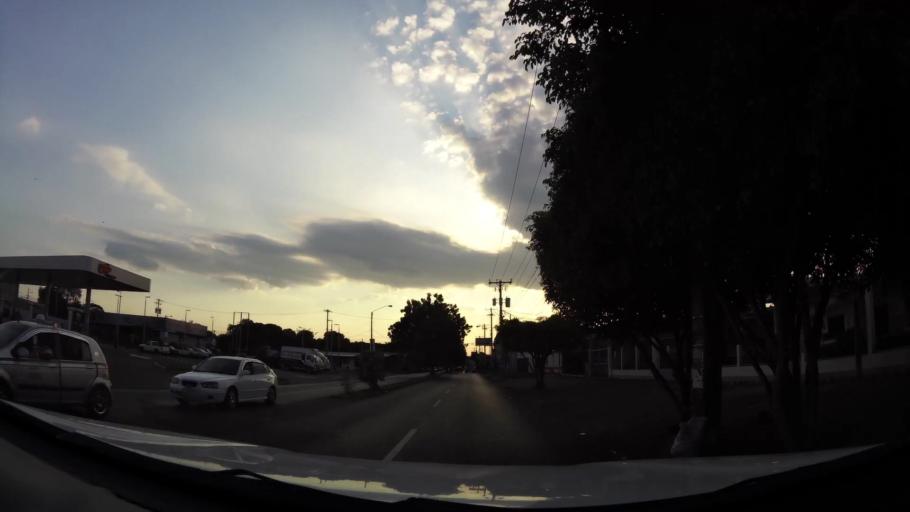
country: NI
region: Managua
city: Managua
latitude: 12.1461
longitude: -86.2416
